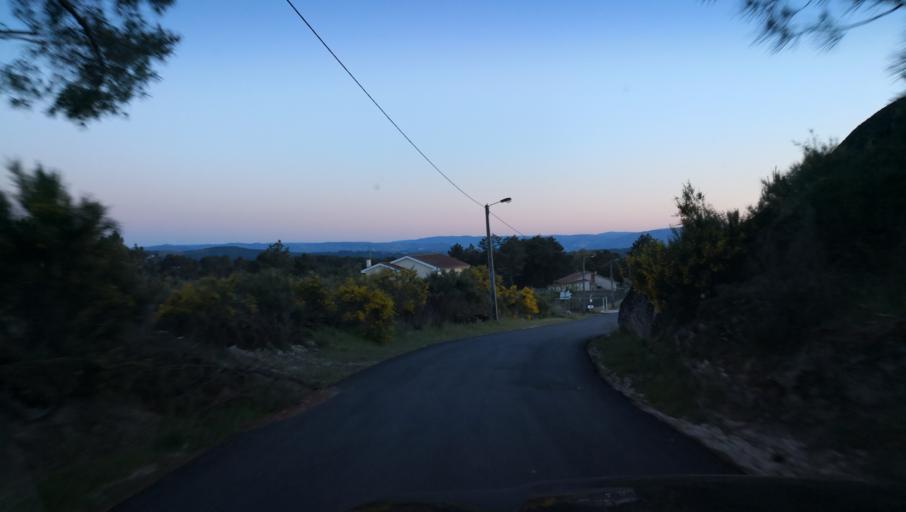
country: PT
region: Vila Real
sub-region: Vila Real
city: Vila Real
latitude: 41.3009
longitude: -7.6705
